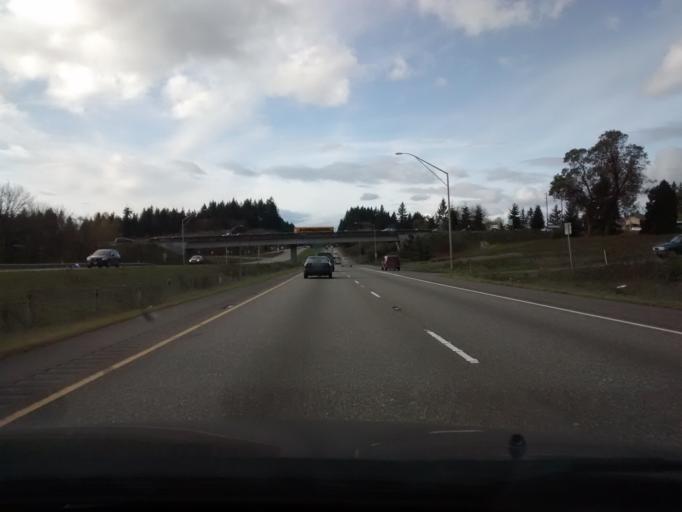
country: US
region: Washington
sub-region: Pierce County
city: Gig Harbor
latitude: 47.3194
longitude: -122.5888
